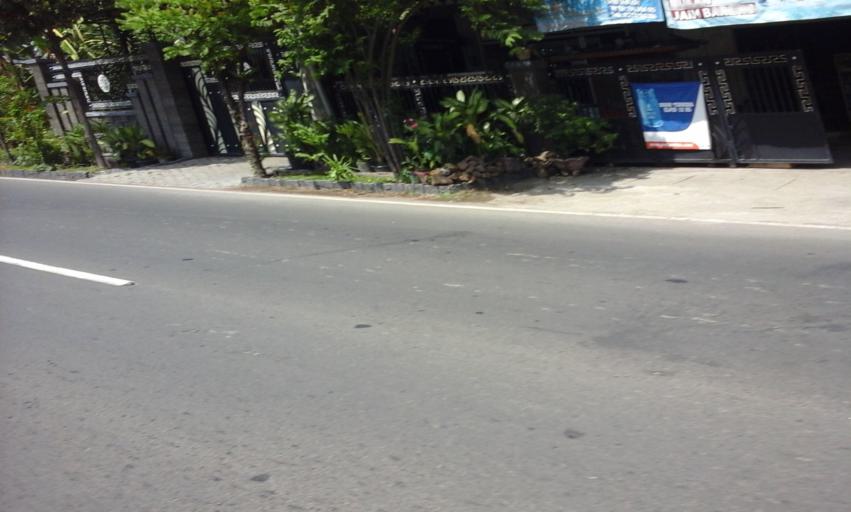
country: ID
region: East Java
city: Klatakan
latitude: -8.1226
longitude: 114.3976
